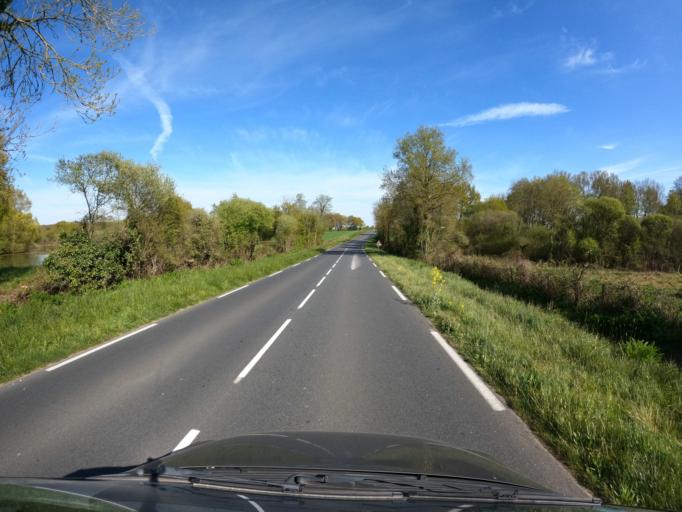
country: FR
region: Pays de la Loire
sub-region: Departement de Maine-et-Loire
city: La Seguiniere
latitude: 47.0738
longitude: -0.9275
